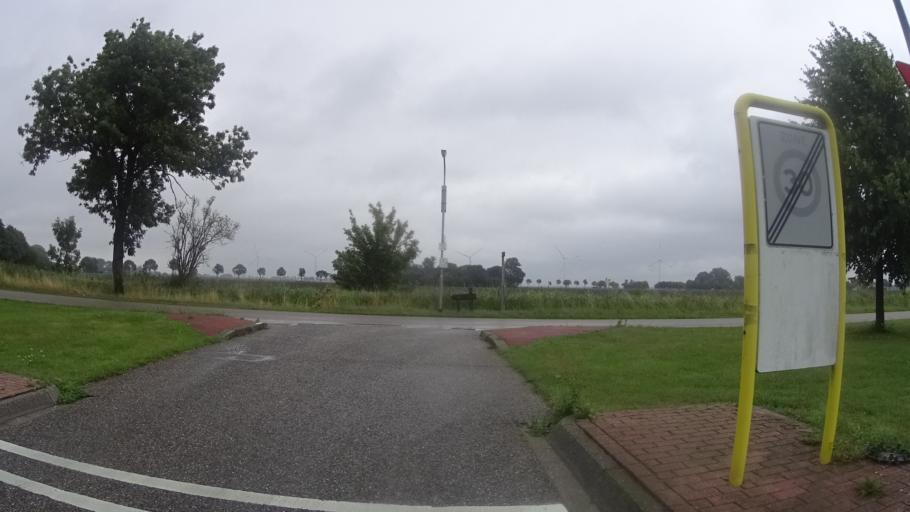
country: DE
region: Lower Saxony
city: Bunde
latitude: 53.1841
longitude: 7.2179
